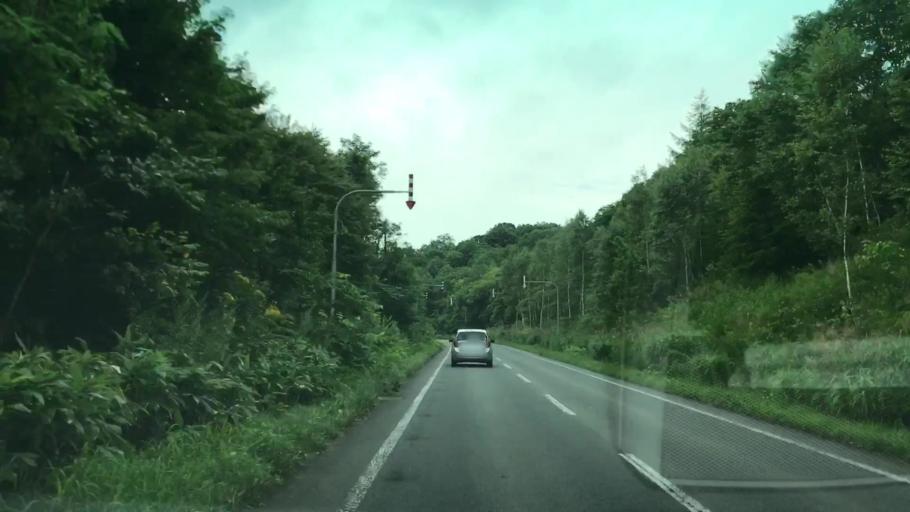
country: JP
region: Hokkaido
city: Yoichi
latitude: 43.1434
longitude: 140.8208
